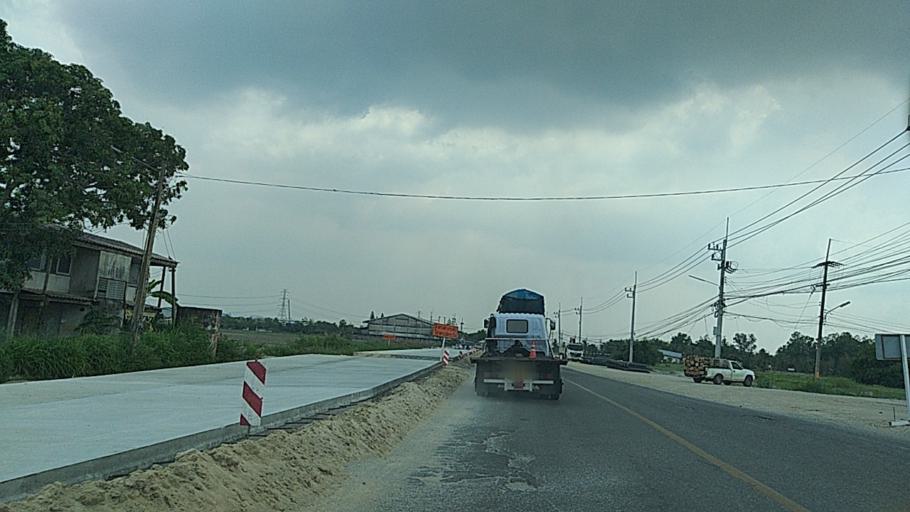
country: TH
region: Chon Buri
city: Ban Bueng
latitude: 13.3157
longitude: 101.1838
